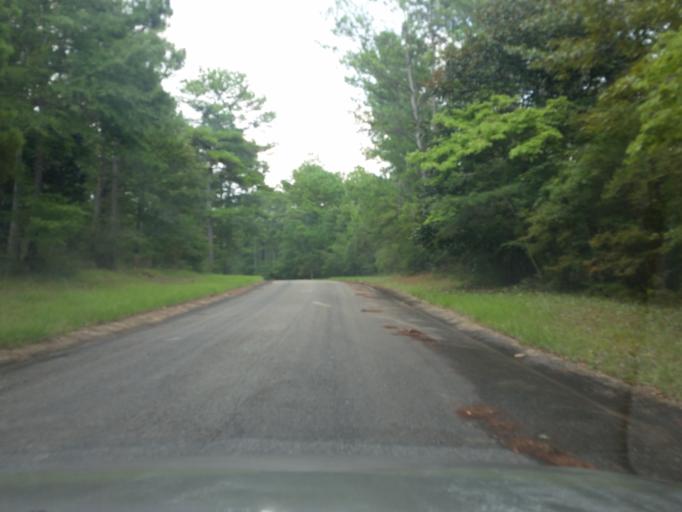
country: US
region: Alabama
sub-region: Baldwin County
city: Spanish Fort
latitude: 30.7317
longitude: -87.9097
